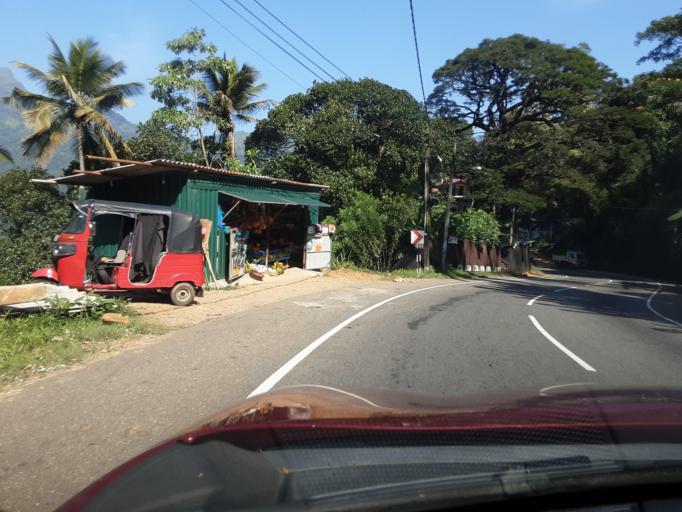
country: LK
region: Uva
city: Badulla
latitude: 7.0189
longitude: 81.0545
